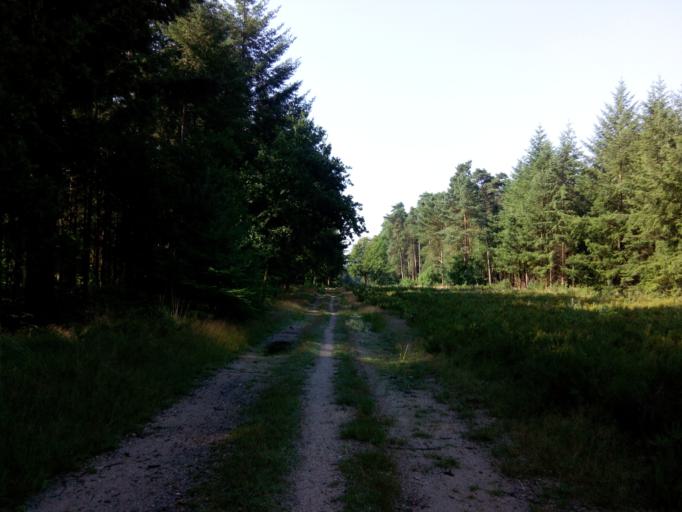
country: NL
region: Utrecht
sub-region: Gemeente Utrechtse Heuvelrug
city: Maarn
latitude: 52.0867
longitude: 5.3545
